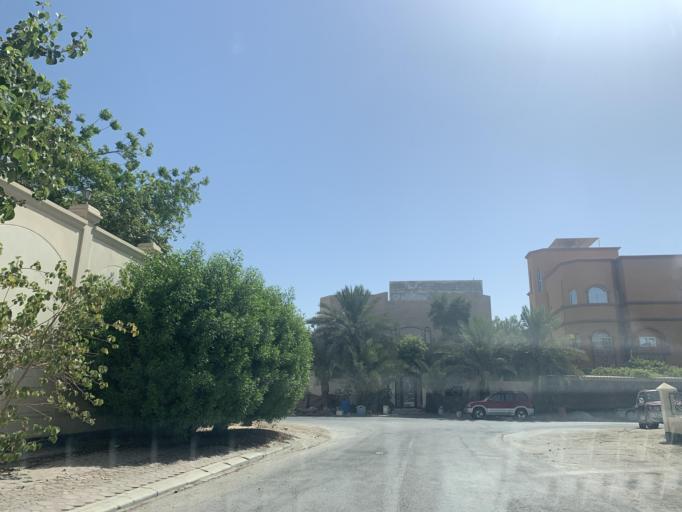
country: BH
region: Manama
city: Jidd Hafs
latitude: 26.2248
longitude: 50.5272
